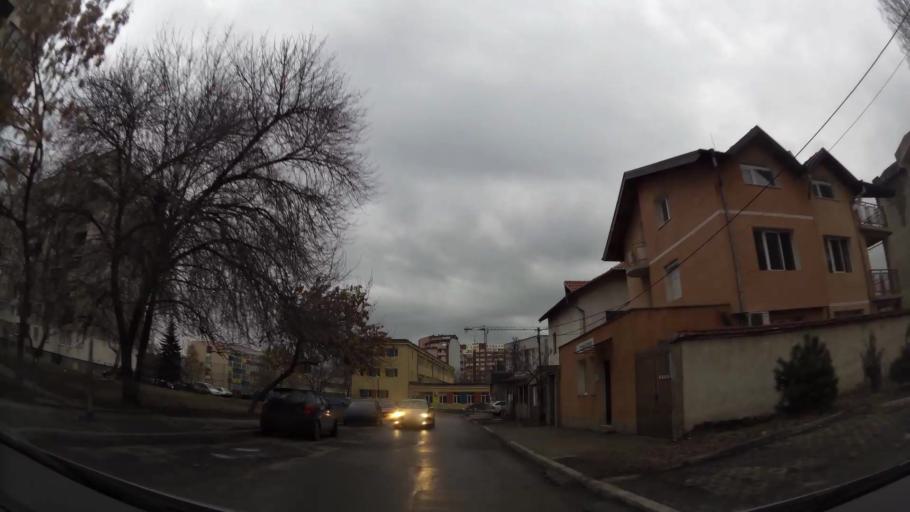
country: BG
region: Sofia-Capital
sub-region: Stolichna Obshtina
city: Sofia
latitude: 42.7268
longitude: 23.2939
